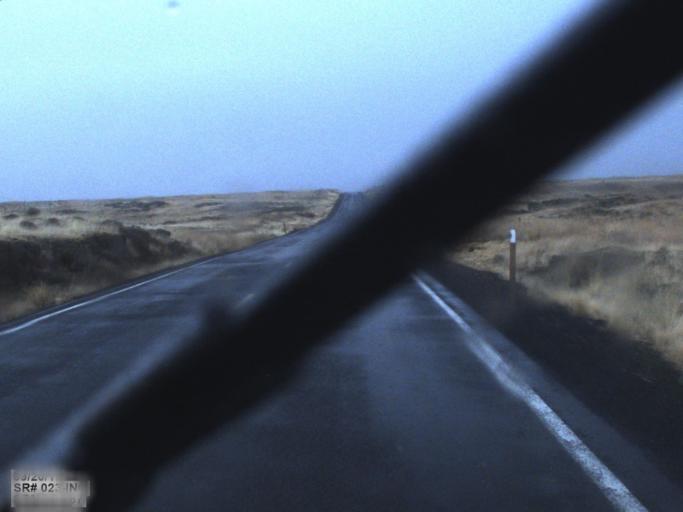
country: US
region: Washington
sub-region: Spokane County
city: Medical Lake
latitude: 47.2172
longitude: -117.8981
